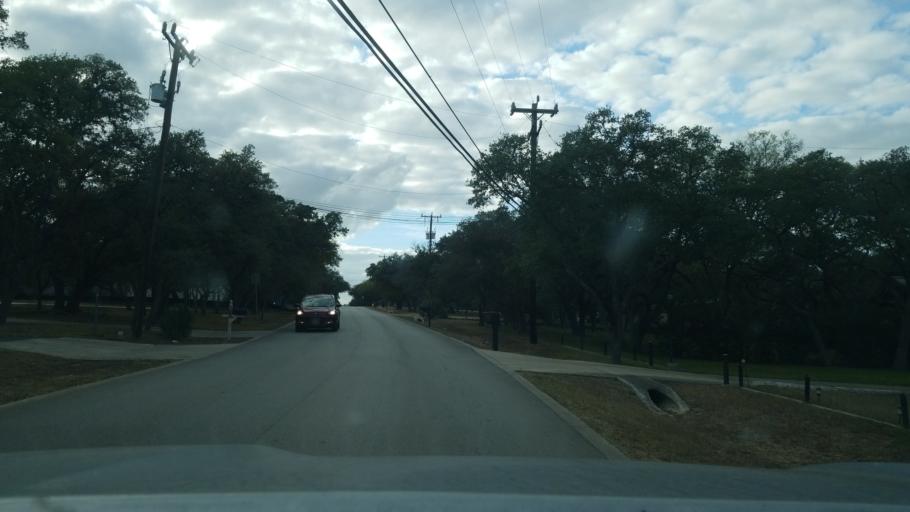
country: US
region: Texas
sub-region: Bexar County
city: Hollywood Park
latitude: 29.5940
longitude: -98.4754
